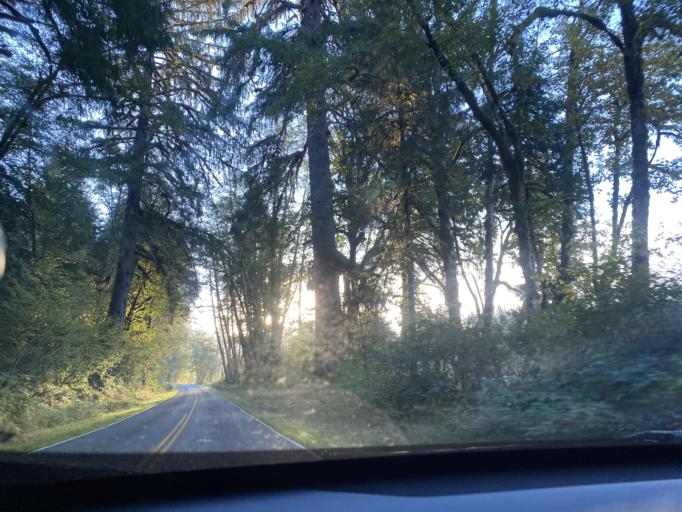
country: US
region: Washington
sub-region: Clallam County
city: Forks
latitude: 47.8225
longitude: -124.1968
